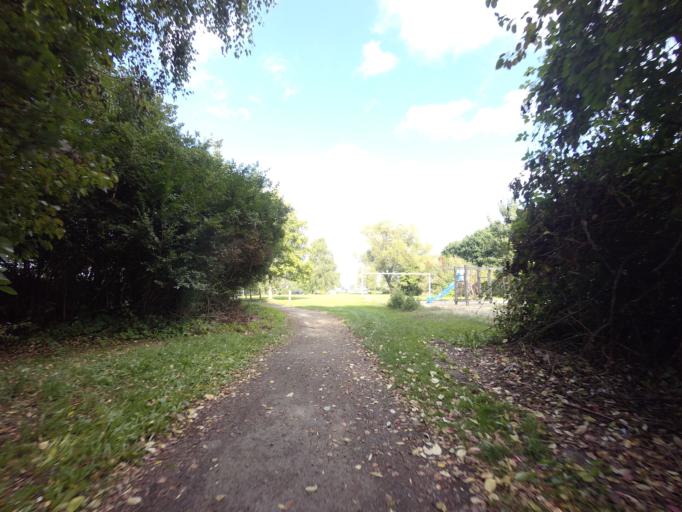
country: BE
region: Flanders
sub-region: Provincie Antwerpen
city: Aartselaar
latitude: 51.1154
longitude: 4.4017
